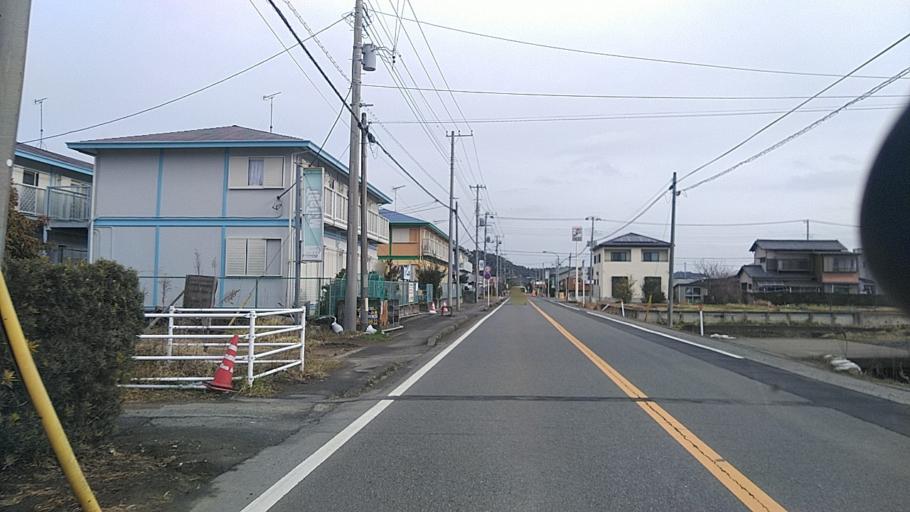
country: JP
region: Chiba
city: Naruto
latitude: 35.5879
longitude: 140.3843
